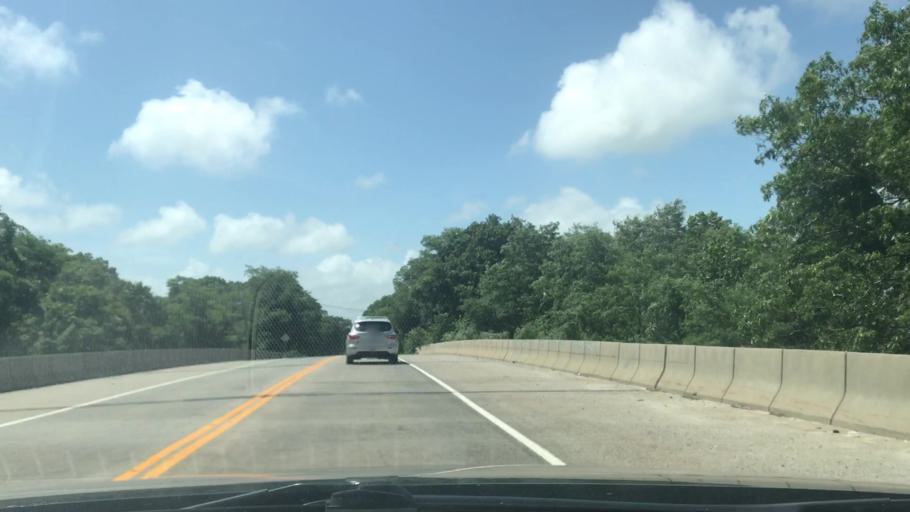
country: US
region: New York
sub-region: Suffolk County
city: Calverton
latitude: 40.9163
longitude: -72.7092
